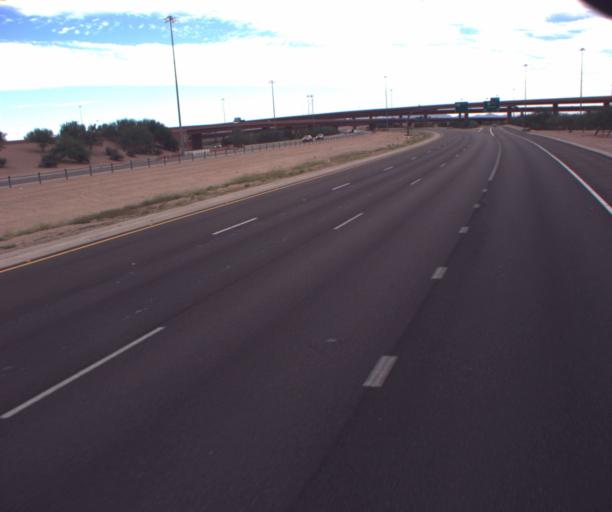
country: US
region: Arizona
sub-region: Pinal County
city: Apache Junction
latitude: 33.3921
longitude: -111.6470
